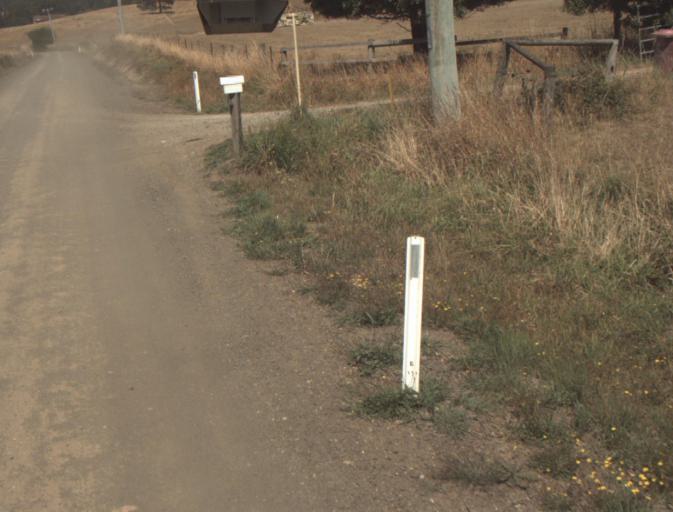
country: AU
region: Tasmania
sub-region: Launceston
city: Mayfield
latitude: -41.2542
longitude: 147.1332
